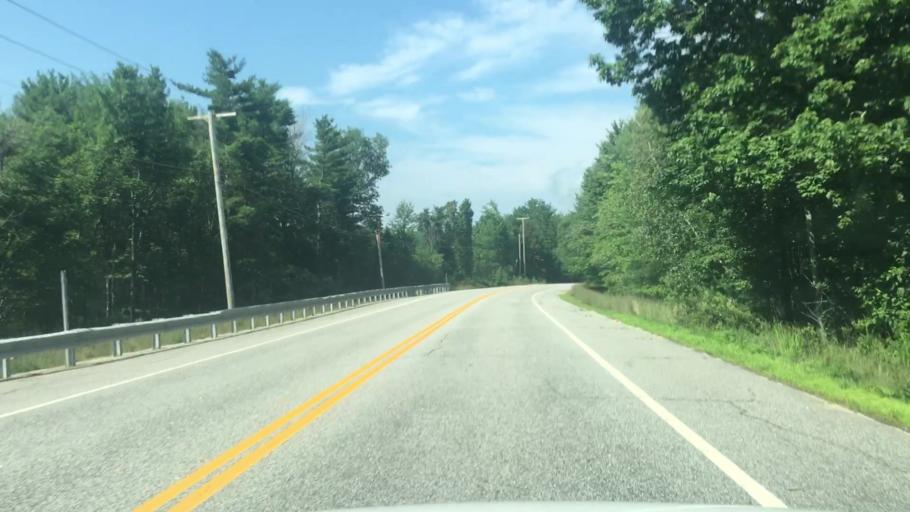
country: US
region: Maine
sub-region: Oxford County
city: West Paris
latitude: 44.3337
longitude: -70.5440
